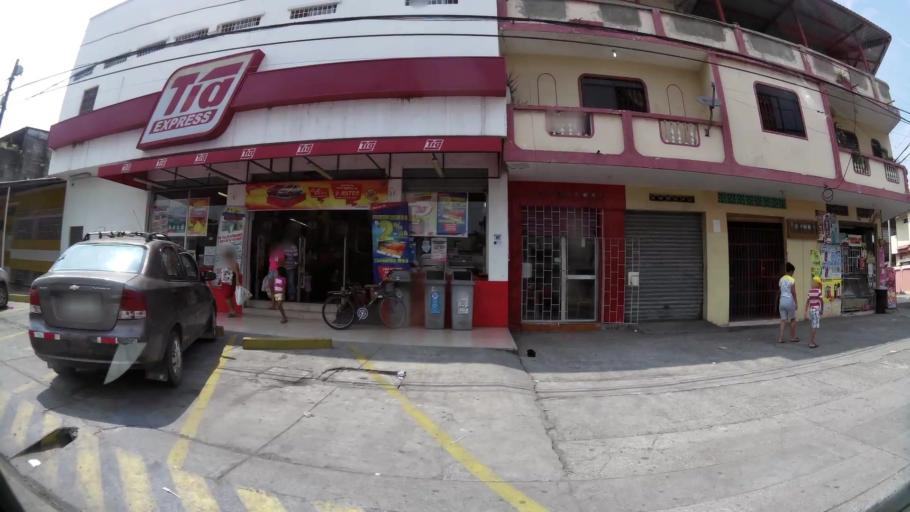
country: EC
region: Guayas
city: Guayaquil
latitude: -2.2462
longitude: -79.8904
